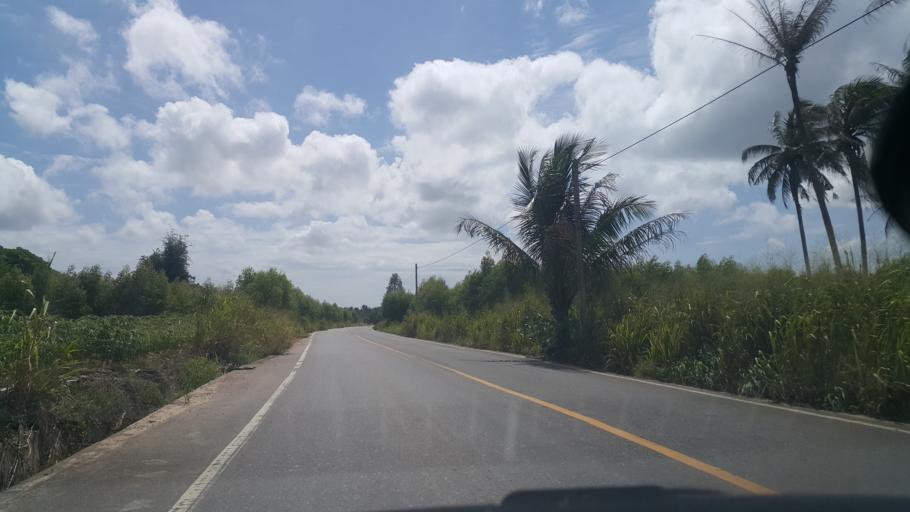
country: TH
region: Rayong
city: Ban Chang
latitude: 12.8063
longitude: 101.0137
